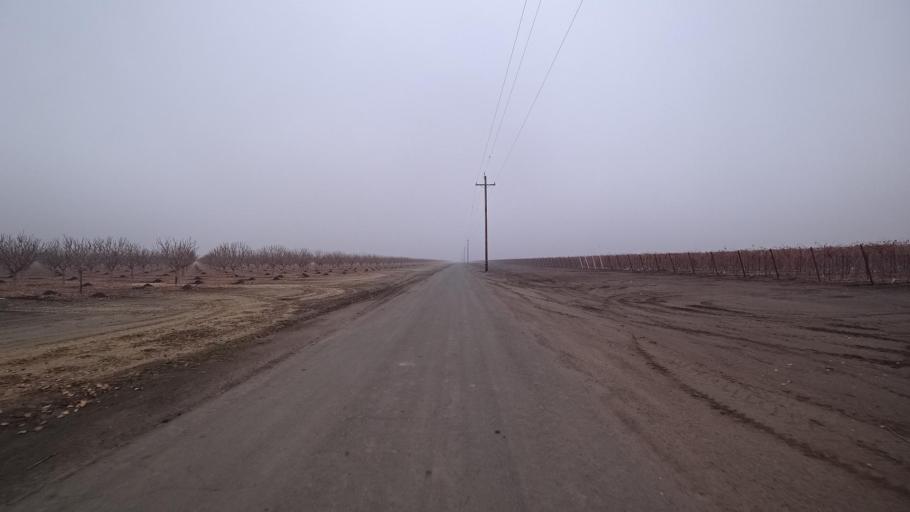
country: US
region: California
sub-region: Kern County
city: Buttonwillow
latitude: 35.4269
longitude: -119.5321
